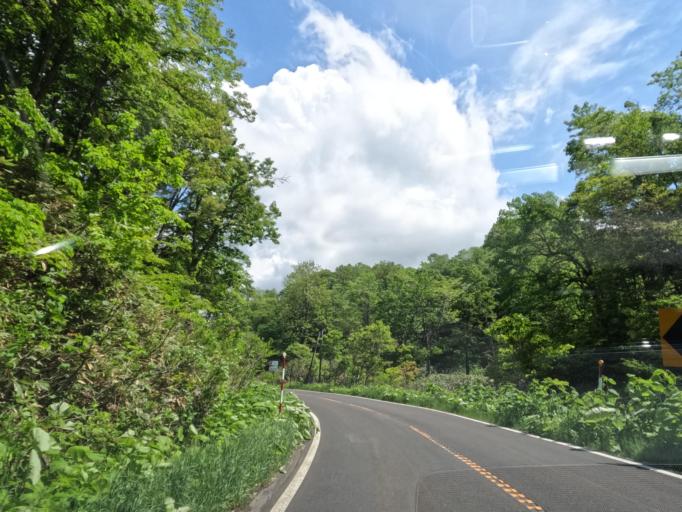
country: JP
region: Hokkaido
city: Takikawa
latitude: 43.5447
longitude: 141.6290
